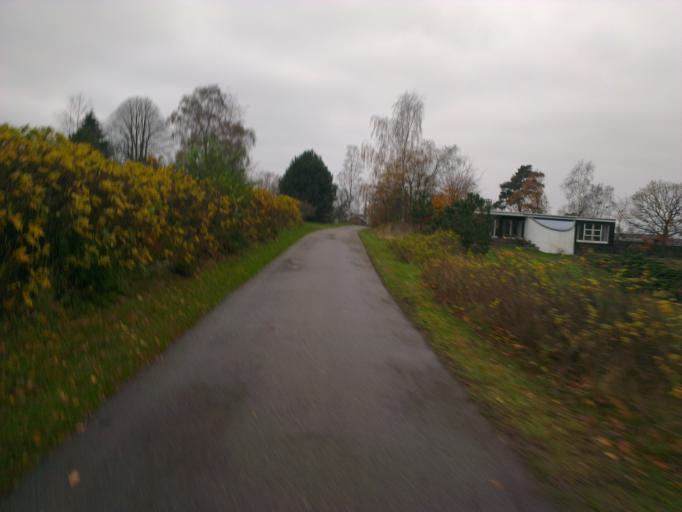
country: DK
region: Capital Region
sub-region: Frederikssund Kommune
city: Jaegerspris
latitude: 55.8507
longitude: 12.0060
